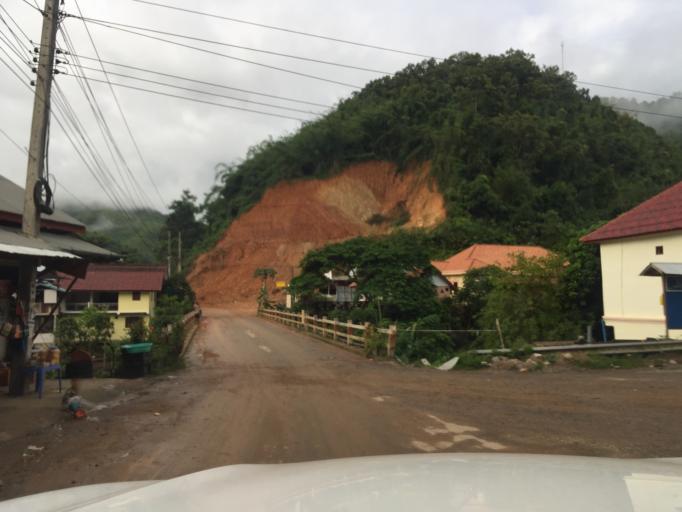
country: LA
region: Phongsali
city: Khoa
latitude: 21.1019
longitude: 102.2540
